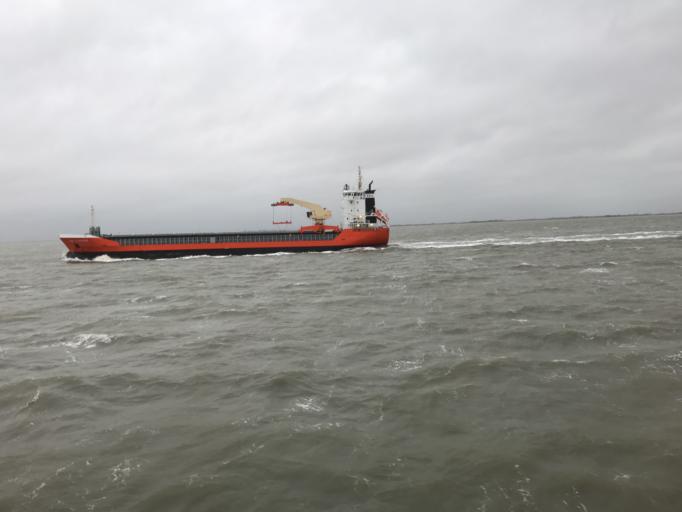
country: NL
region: Groningen
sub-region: Gemeente Delfzijl
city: Delfzijl
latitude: 53.3925
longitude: 6.9554
